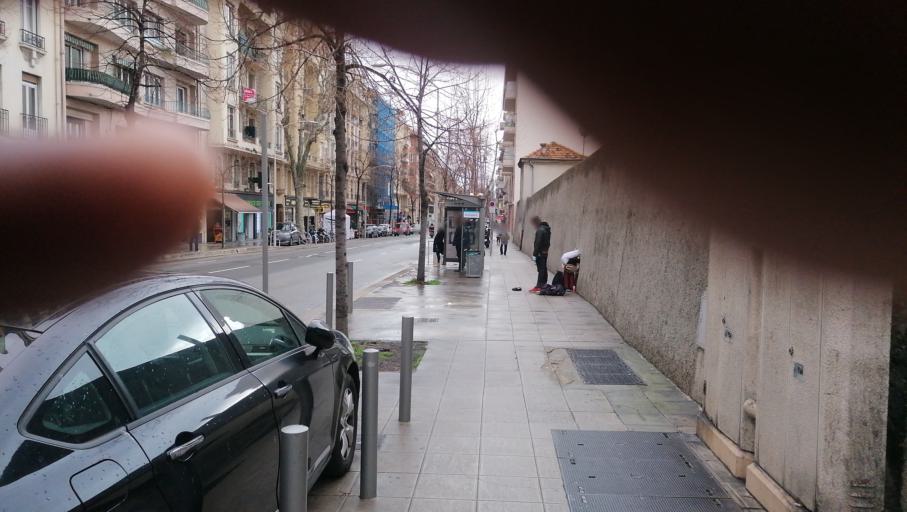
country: FR
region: Provence-Alpes-Cote d'Azur
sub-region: Departement des Alpes-Maritimes
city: Nice
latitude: 43.7094
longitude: 7.2559
